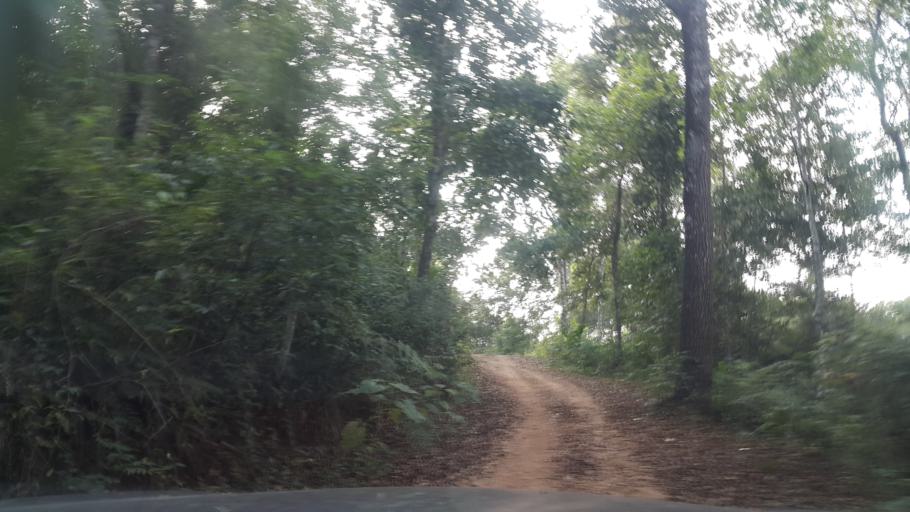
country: TH
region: Chiang Mai
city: Samoeng
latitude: 19.0323
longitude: 98.6511
